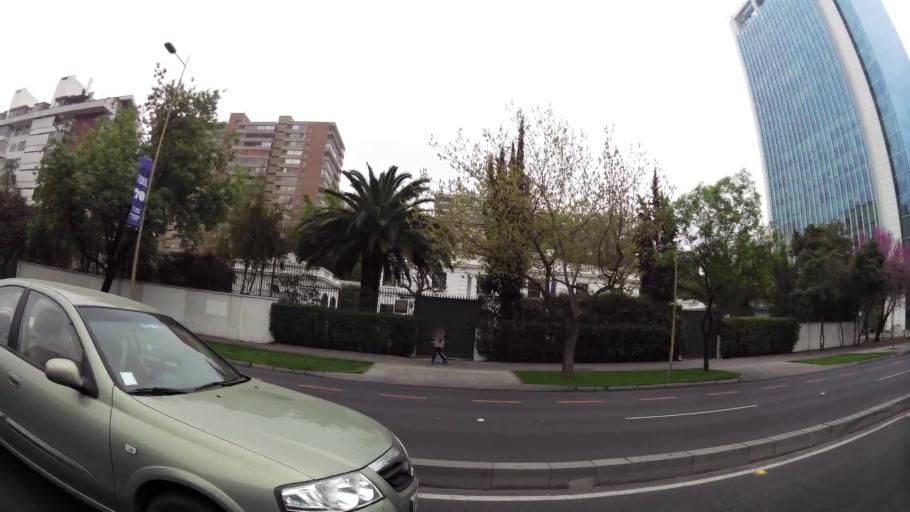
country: CL
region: Santiago Metropolitan
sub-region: Provincia de Santiago
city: Villa Presidente Frei, Nunoa, Santiago, Chile
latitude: -33.4105
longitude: -70.5731
